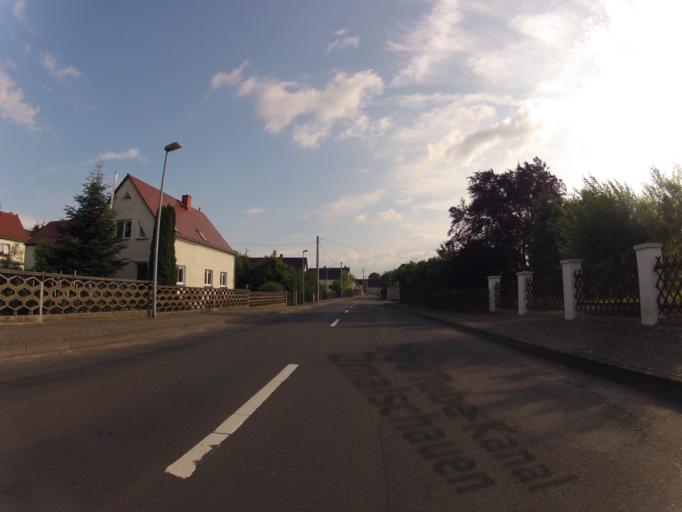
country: DE
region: Saxony
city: Falkenhain
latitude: 51.4018
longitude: 12.8714
